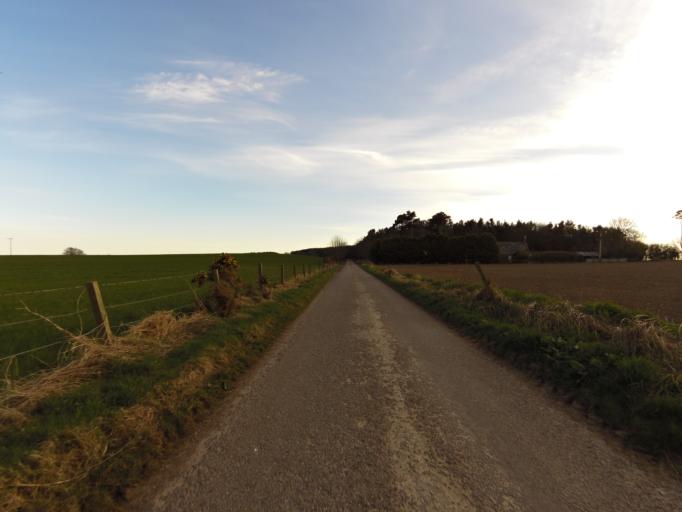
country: GB
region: Scotland
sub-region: Aberdeenshire
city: Stonehaven
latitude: 56.9295
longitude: -2.2277
